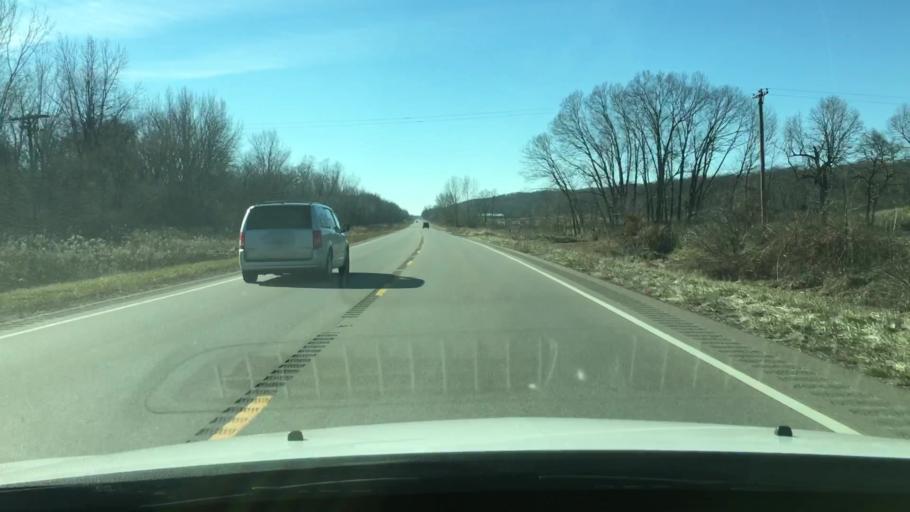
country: US
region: Illinois
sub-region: Peoria County
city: Glasford
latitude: 40.5463
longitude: -89.8576
